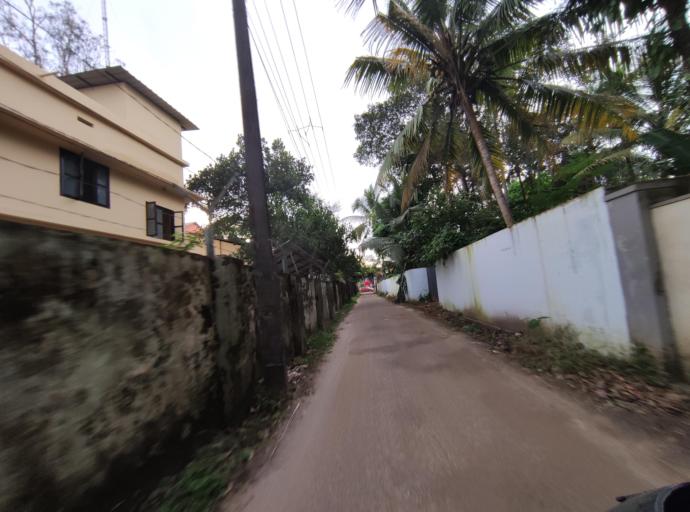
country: IN
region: Kerala
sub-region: Alappuzha
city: Shertallai
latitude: 9.6694
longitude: 76.3403
